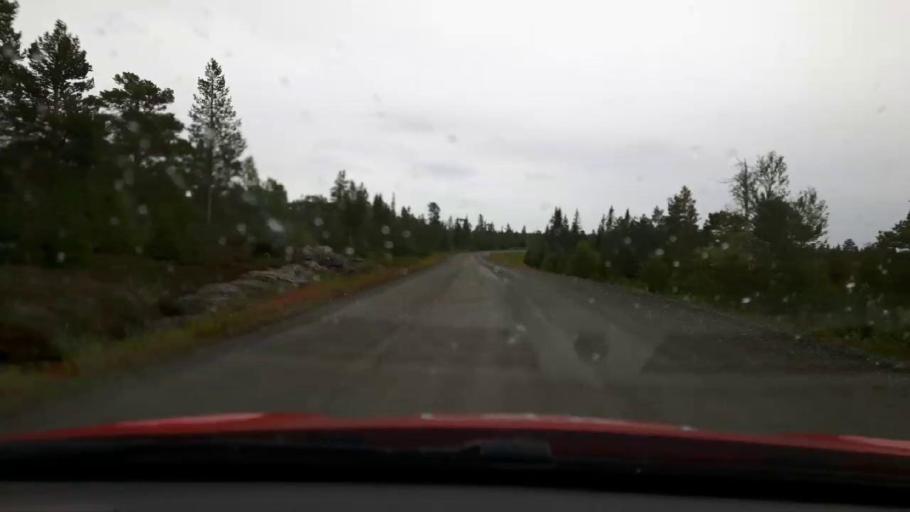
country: NO
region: Nord-Trondelag
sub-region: Meraker
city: Meraker
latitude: 63.6377
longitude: 12.2759
